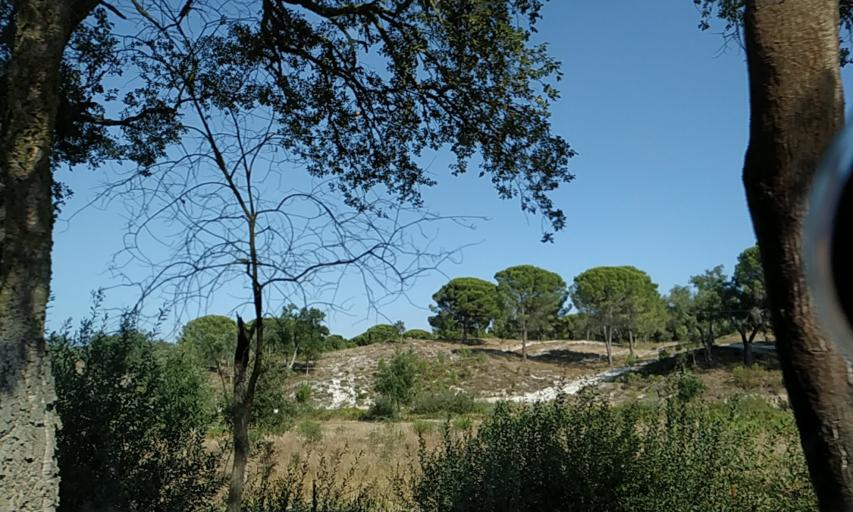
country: PT
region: Evora
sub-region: Vendas Novas
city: Vendas Novas
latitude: 38.7911
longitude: -8.5809
